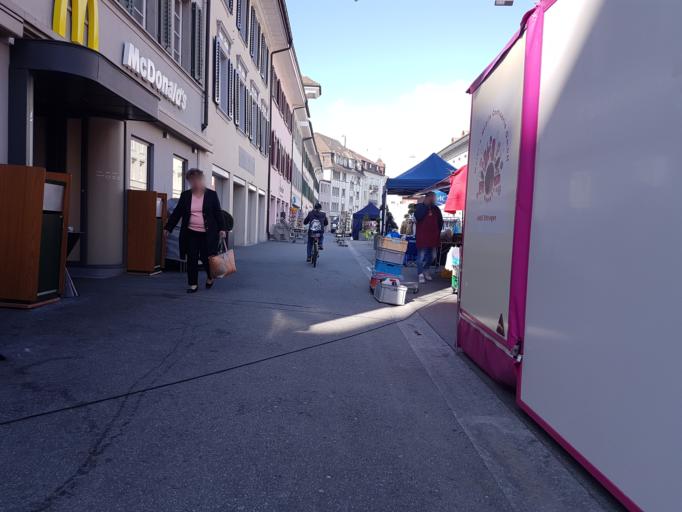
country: CH
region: Solothurn
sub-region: Bezirk Olten
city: Olten
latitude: 47.3500
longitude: 7.9024
